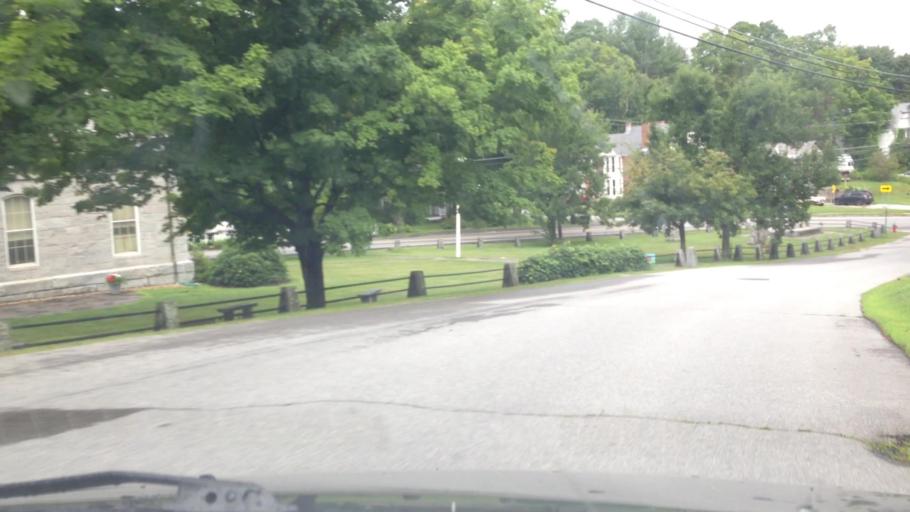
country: US
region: New Hampshire
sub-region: Cheshire County
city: Marlborough
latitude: 42.9016
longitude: -72.2055
